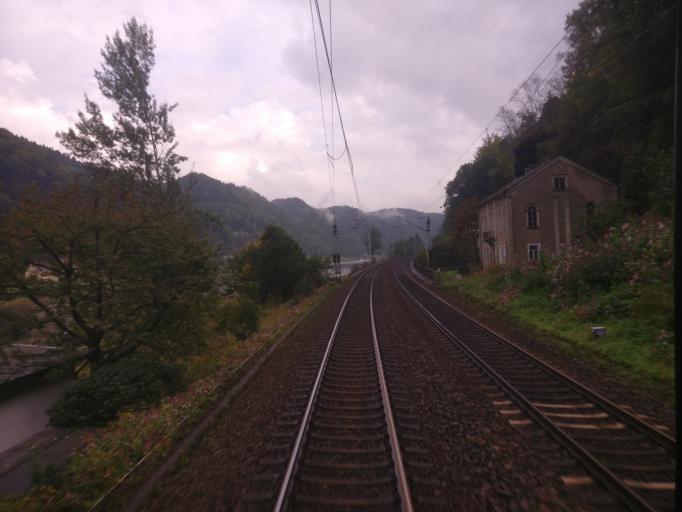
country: DE
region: Saxony
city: Bad Schandau
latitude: 50.8963
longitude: 14.2224
